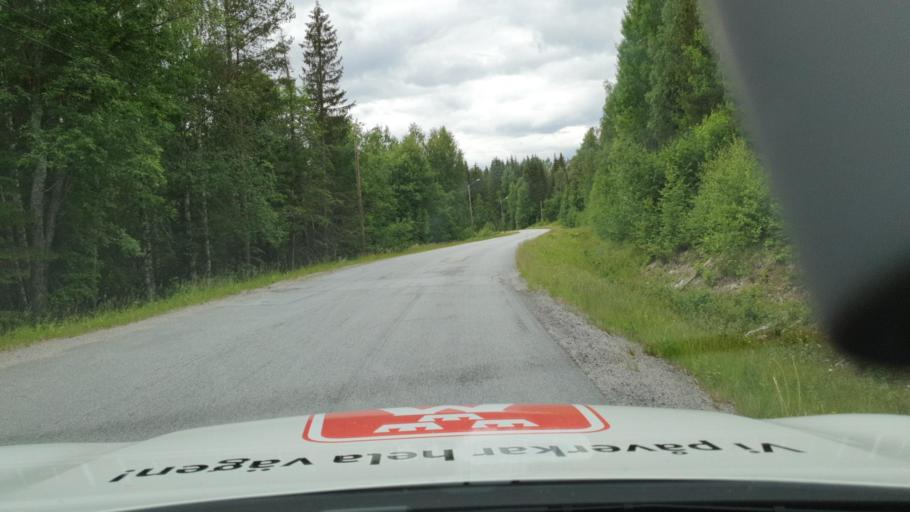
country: SE
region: Vaesterbotten
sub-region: Bjurholms Kommun
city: Bjurholm
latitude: 63.7807
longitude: 19.2225
